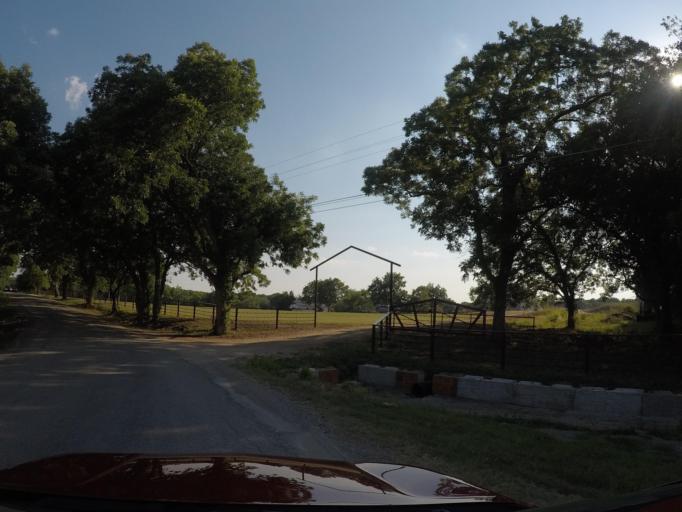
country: US
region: Texas
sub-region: Grayson County
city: Pottsboro
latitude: 33.8031
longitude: -96.6065
